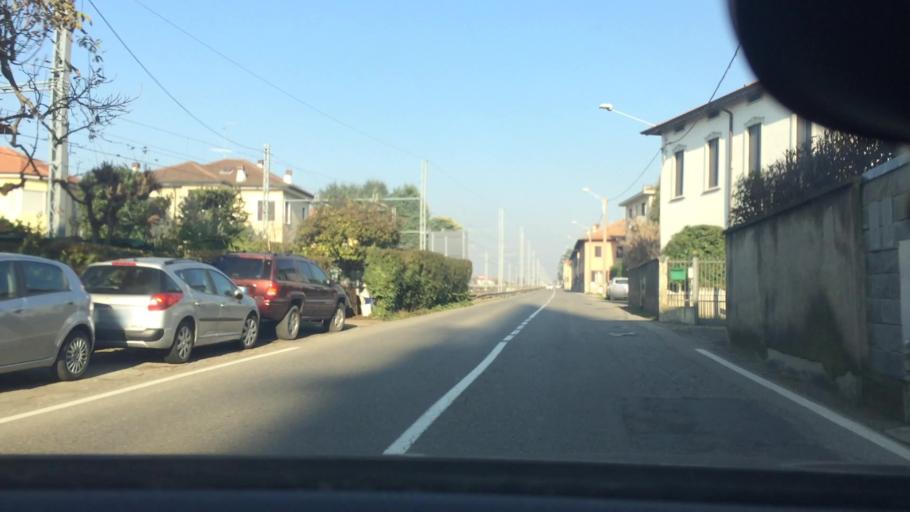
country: IT
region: Lombardy
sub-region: Provincia di Como
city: Rovello Porro
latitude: 45.6540
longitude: 9.0374
